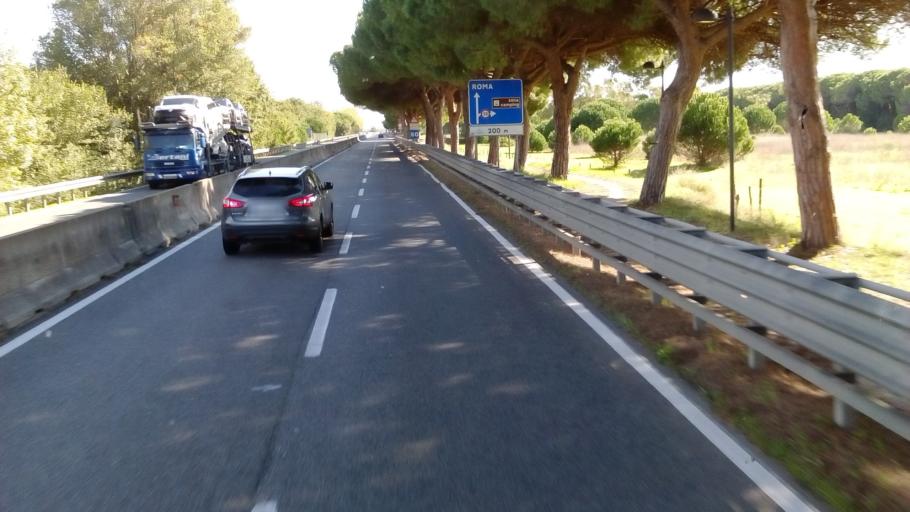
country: IT
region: Tuscany
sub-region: Provincia di Grosseto
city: Fonteblanda
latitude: 42.5410
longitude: 11.1806
